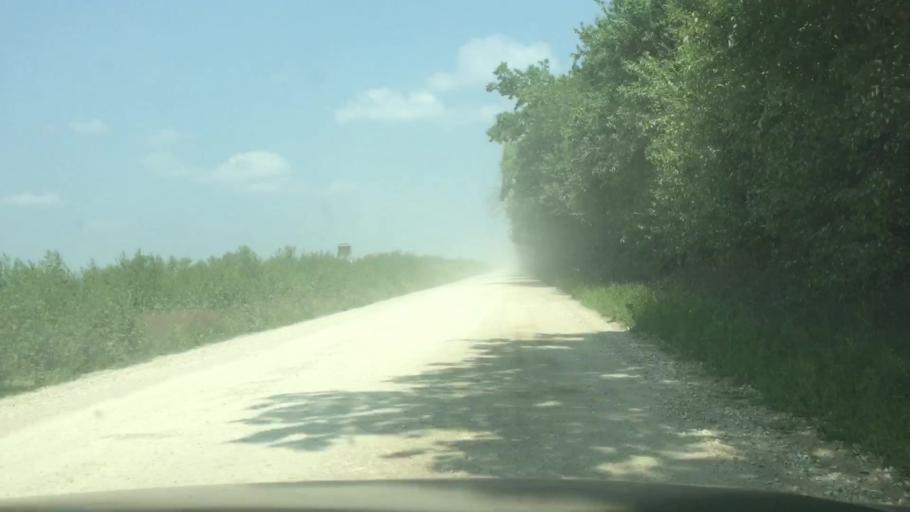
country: US
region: Kansas
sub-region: Allen County
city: Humboldt
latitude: 37.8267
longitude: -95.4093
